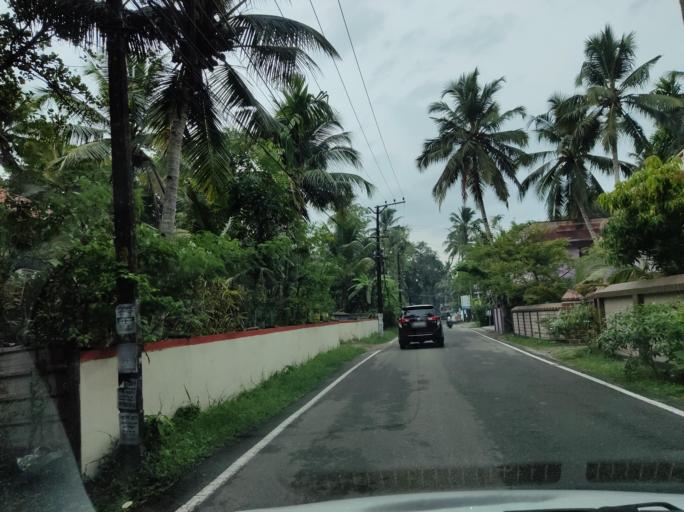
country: IN
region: Kerala
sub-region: Alappuzha
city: Kayankulam
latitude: 9.2011
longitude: 76.4645
